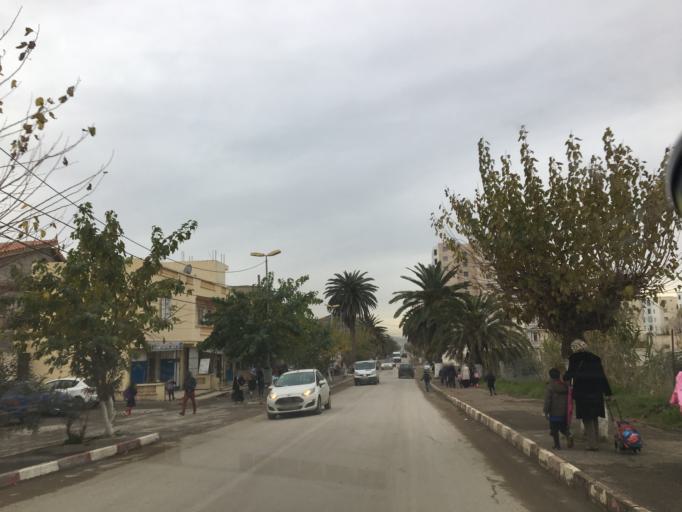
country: DZ
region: Alger
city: Ain Taya
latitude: 36.7910
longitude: 3.2461
